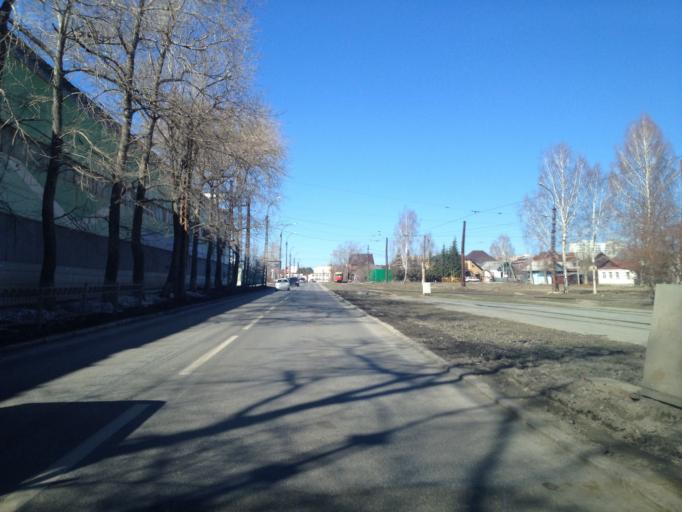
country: RU
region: Sverdlovsk
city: Sovkhoznyy
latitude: 56.7568
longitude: 60.5956
